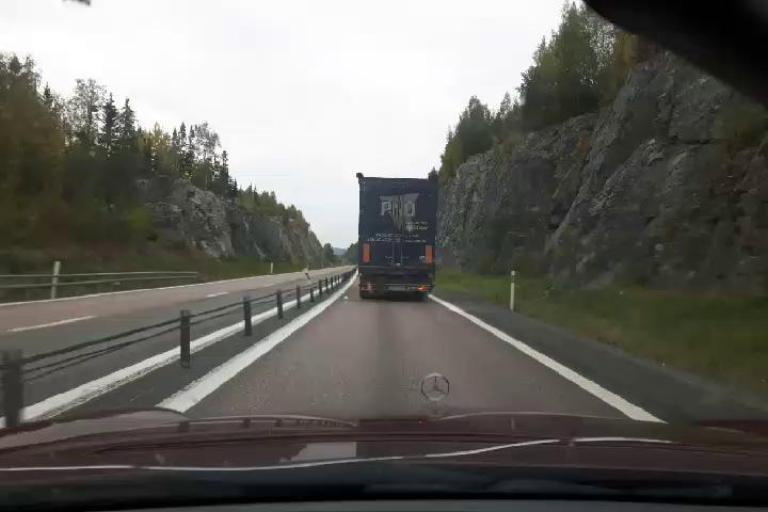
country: SE
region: Vaesternorrland
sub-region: Haernoesands Kommun
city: Haernoesand
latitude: 62.8290
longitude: 17.9680
